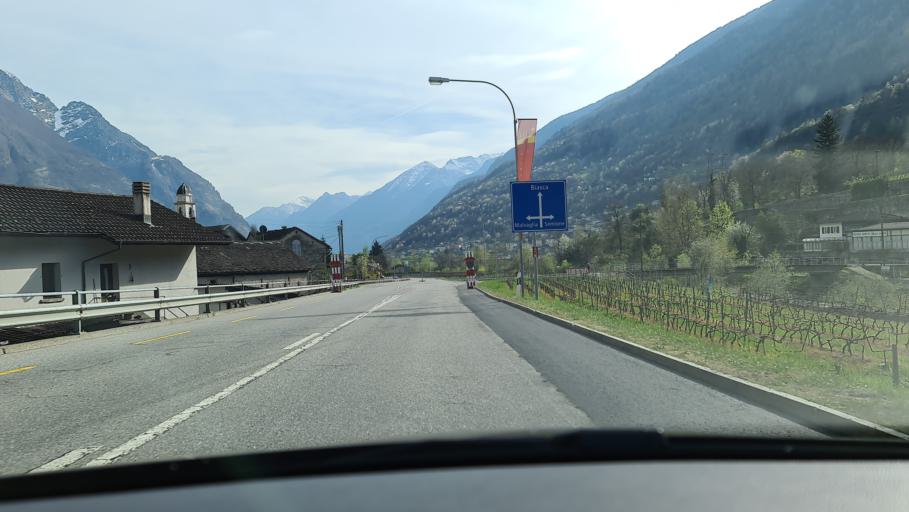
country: CH
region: Ticino
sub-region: Blenio District
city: Malvaglia
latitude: 46.4166
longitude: 8.9777
